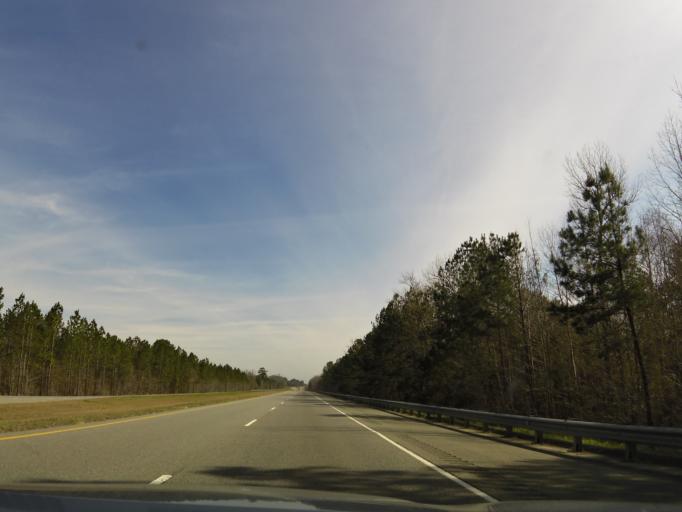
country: US
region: Georgia
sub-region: Lanier County
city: Lakeland
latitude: 30.9280
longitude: -83.0276
